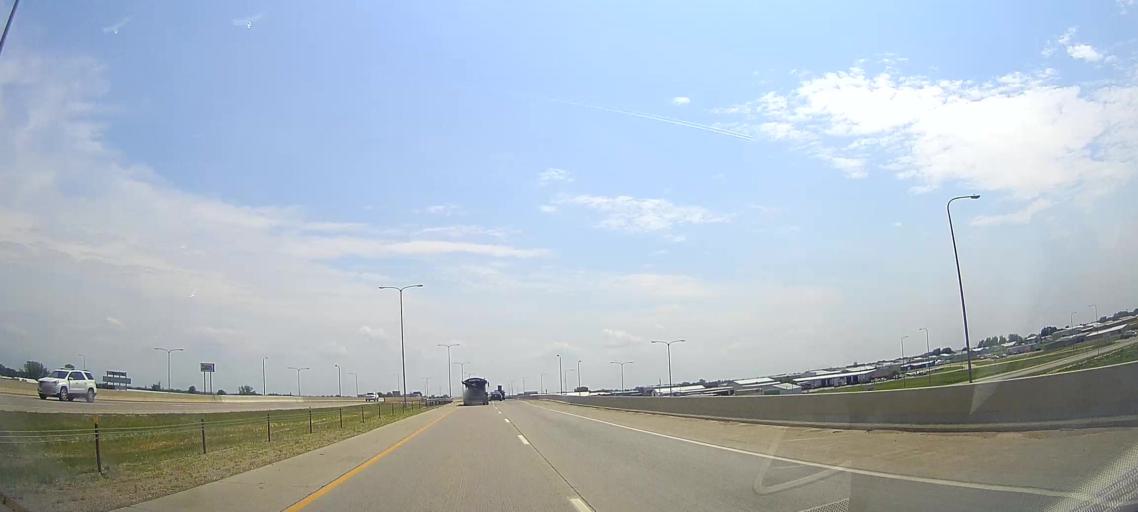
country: US
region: South Dakota
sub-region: Lincoln County
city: Tea
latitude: 43.4618
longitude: -96.7977
